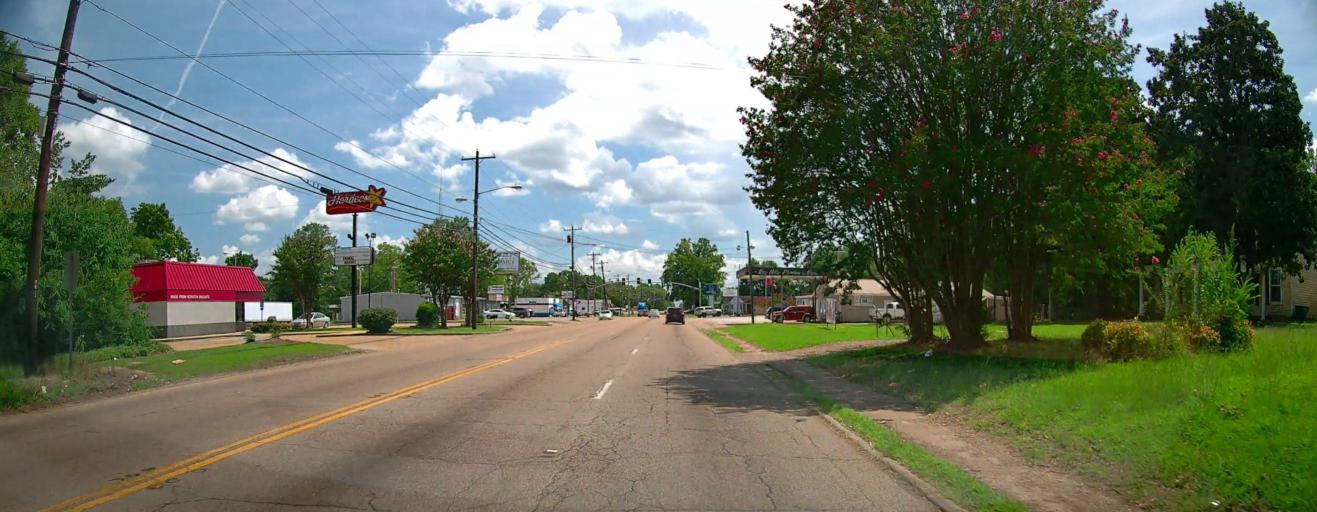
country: US
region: Mississippi
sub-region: Lee County
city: Verona
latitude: 34.1953
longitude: -88.7200
